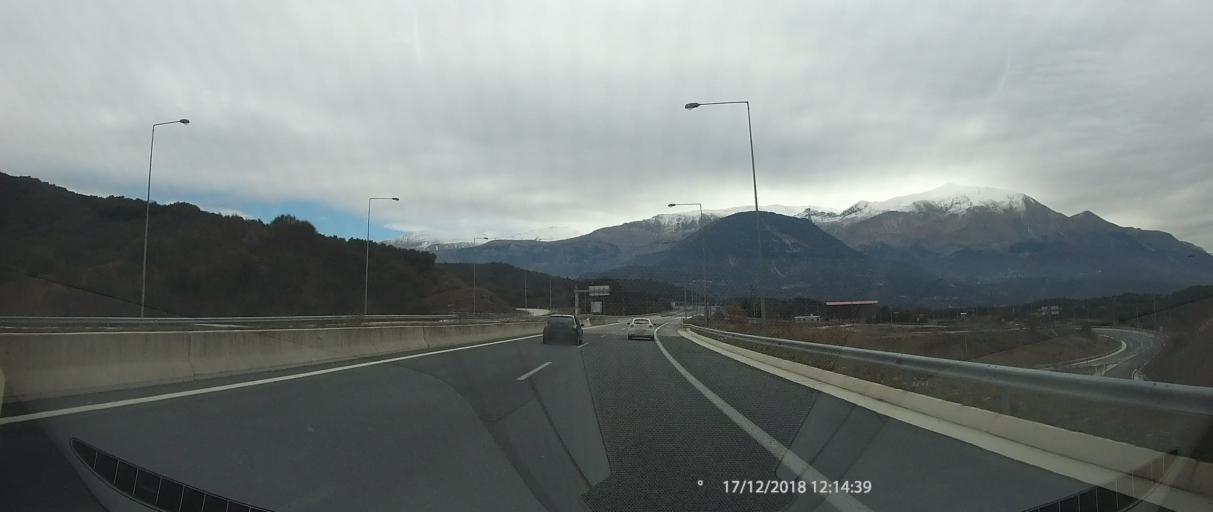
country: GR
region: Epirus
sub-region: Nomos Ioanninon
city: Katsikas
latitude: 39.7178
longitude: 21.0027
